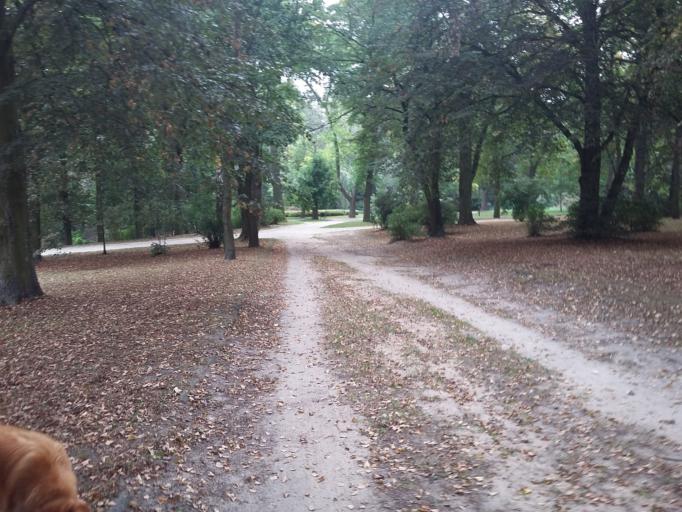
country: PL
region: Lodz Voivodeship
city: Lodz
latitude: 51.7673
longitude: 19.4143
